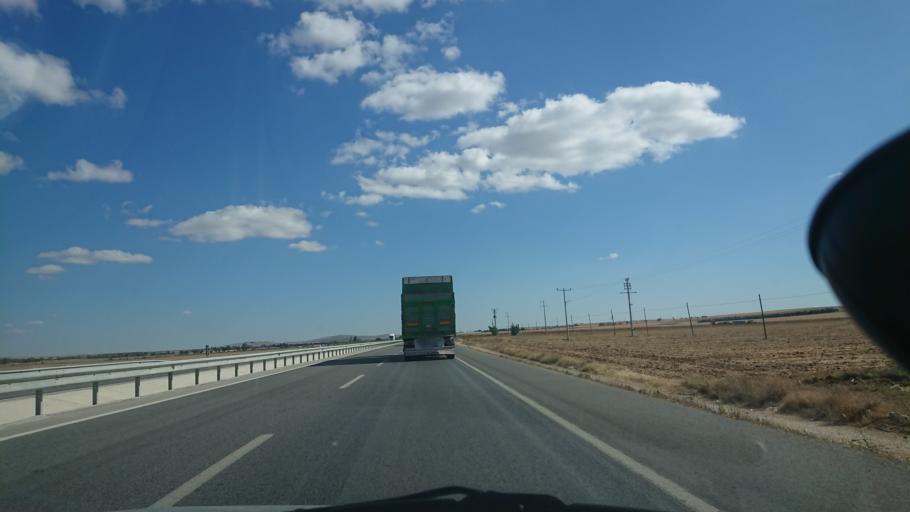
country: TR
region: Eskisehir
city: Mahmudiye
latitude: 39.5527
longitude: 30.9246
